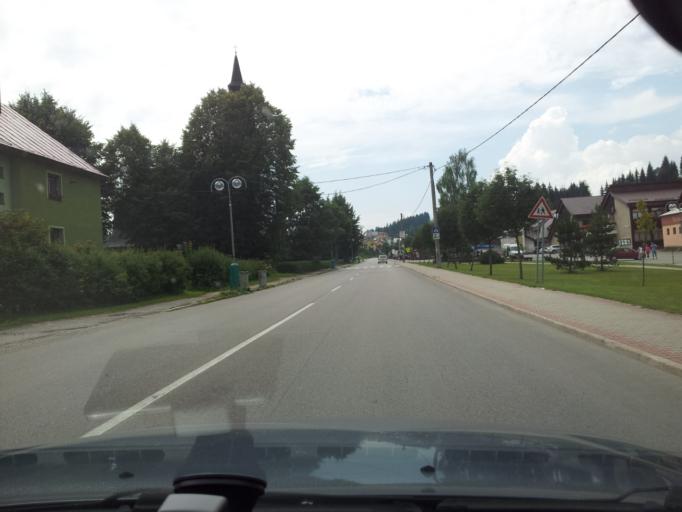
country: SK
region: Zilinsky
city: Oravska Lesna
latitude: 49.3691
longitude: 19.1865
